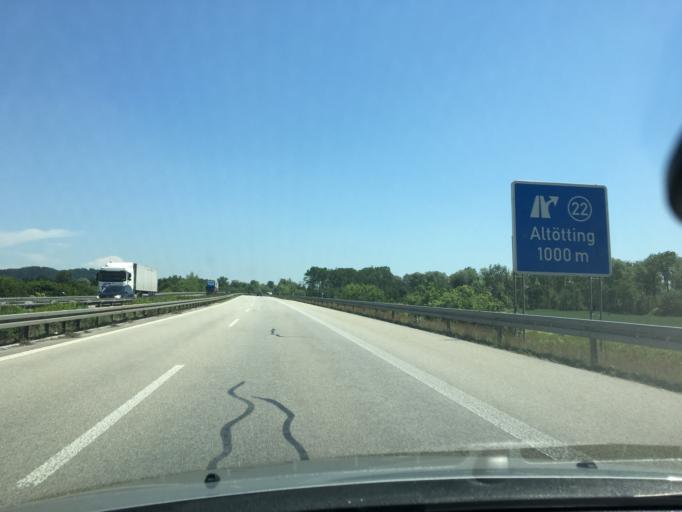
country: DE
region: Bavaria
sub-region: Upper Bavaria
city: Winhoring
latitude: 48.2526
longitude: 12.6441
